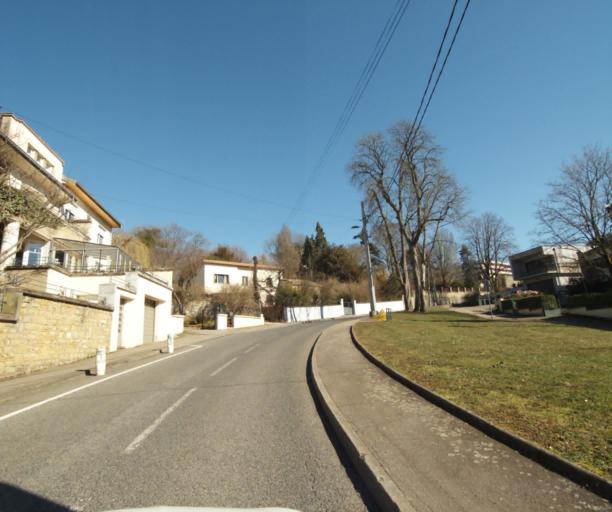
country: FR
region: Lorraine
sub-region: Departement de Meurthe-et-Moselle
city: Malzeville
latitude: 48.7095
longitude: 6.1947
